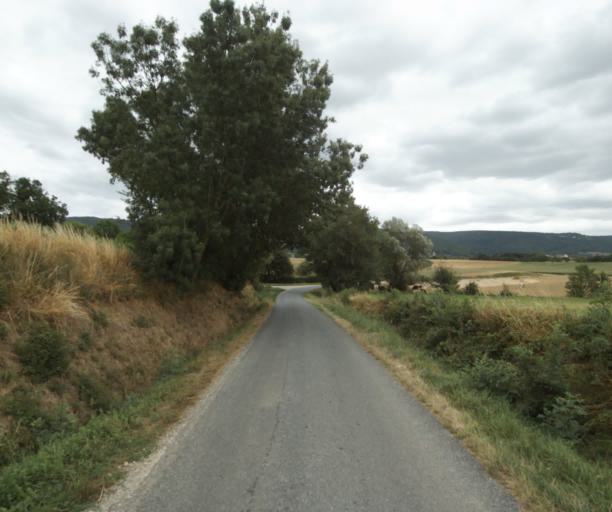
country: FR
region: Midi-Pyrenees
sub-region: Departement du Tarn
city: Soreze
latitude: 43.4671
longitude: 2.0676
